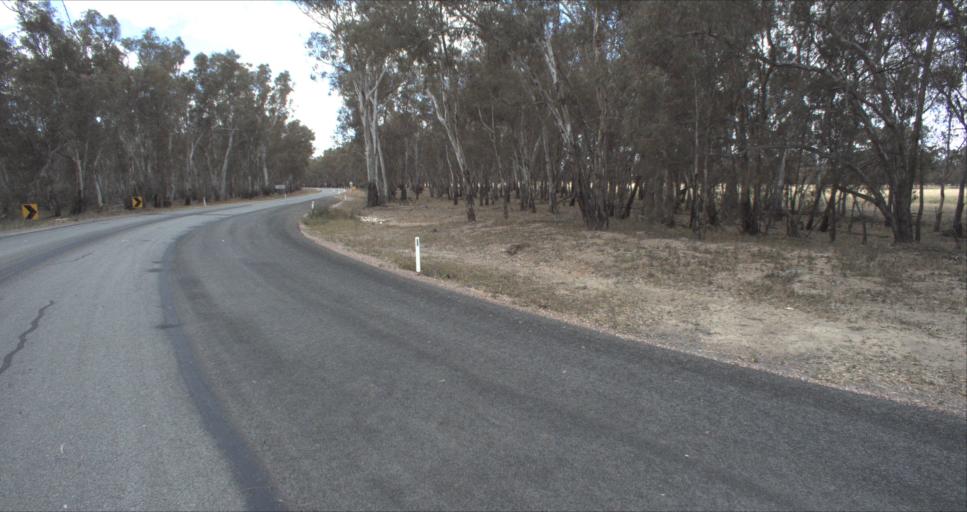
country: AU
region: New South Wales
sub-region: Leeton
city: Leeton
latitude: -34.6318
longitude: 146.3746
